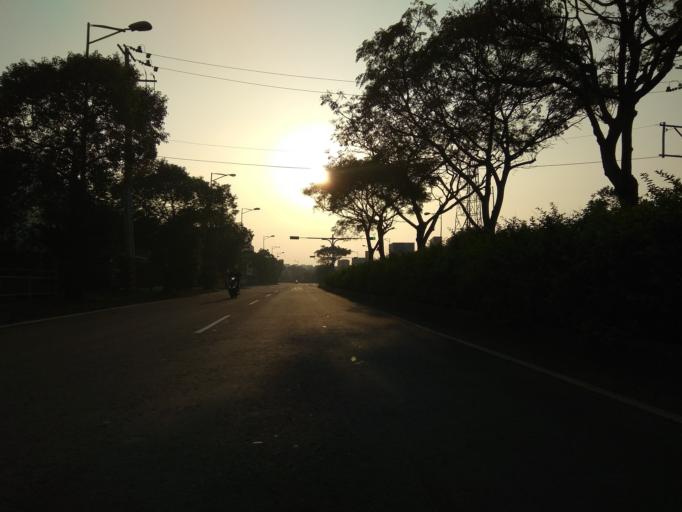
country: TW
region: Taiwan
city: Daxi
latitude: 24.9169
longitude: 121.1763
